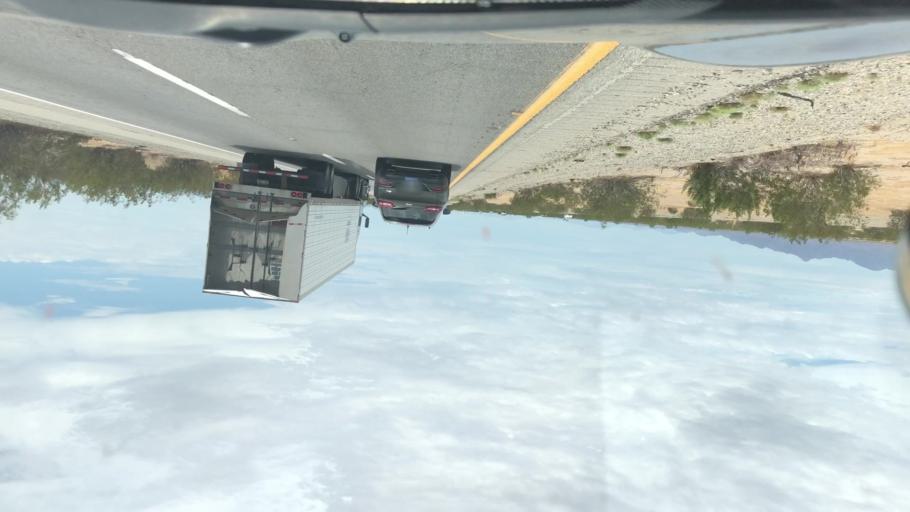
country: US
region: California
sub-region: Riverside County
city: Mesa Verde
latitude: 33.6276
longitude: -115.0630
